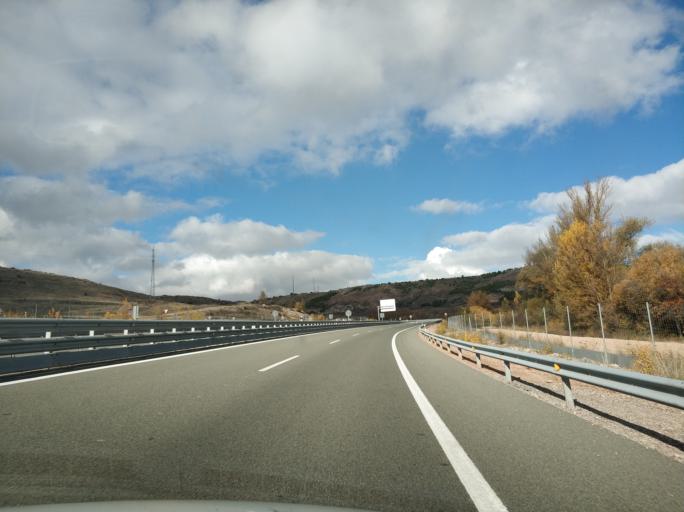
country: ES
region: Castille and Leon
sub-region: Provincia de Soria
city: Medinaceli
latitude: 41.1853
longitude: -2.4309
